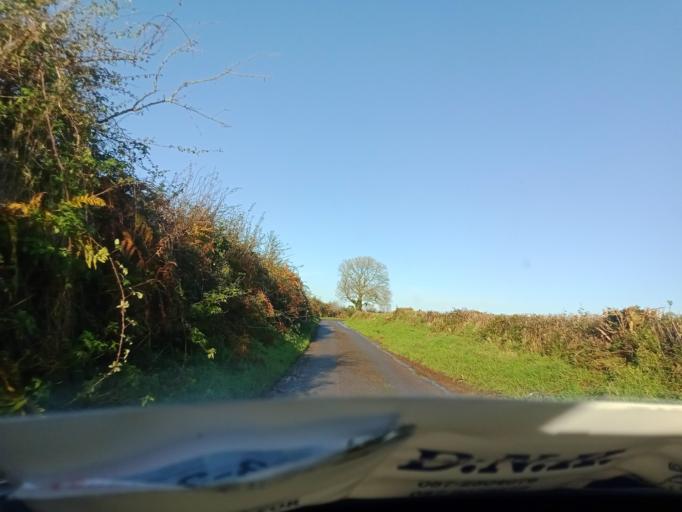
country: IE
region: Munster
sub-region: Waterford
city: Waterford
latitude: 52.2865
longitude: -7.1675
